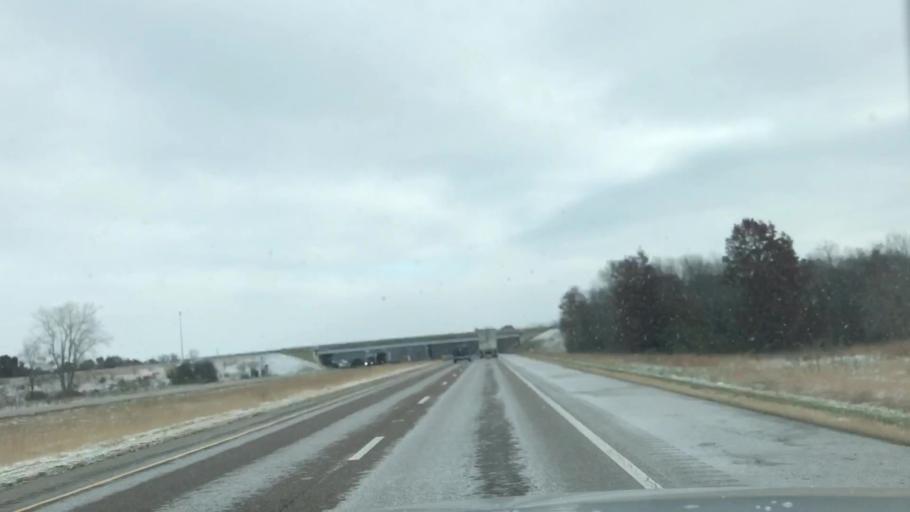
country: US
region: Illinois
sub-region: Macoupin County
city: Staunton
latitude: 38.9657
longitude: -89.7557
